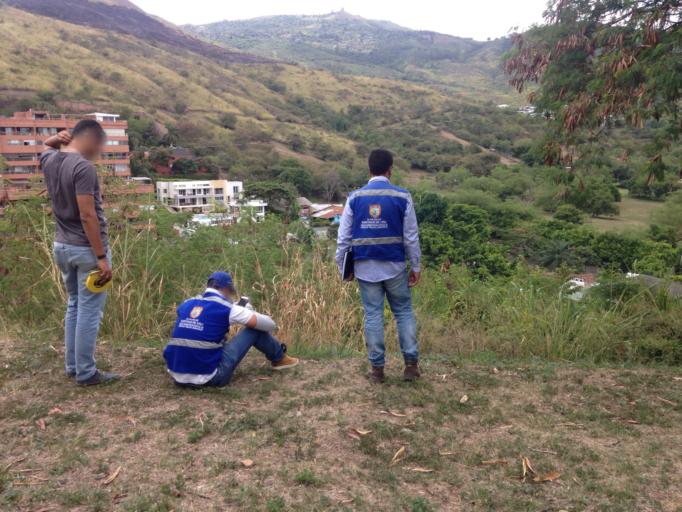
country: CO
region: Valle del Cauca
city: Cali
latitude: 3.4916
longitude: -76.5255
